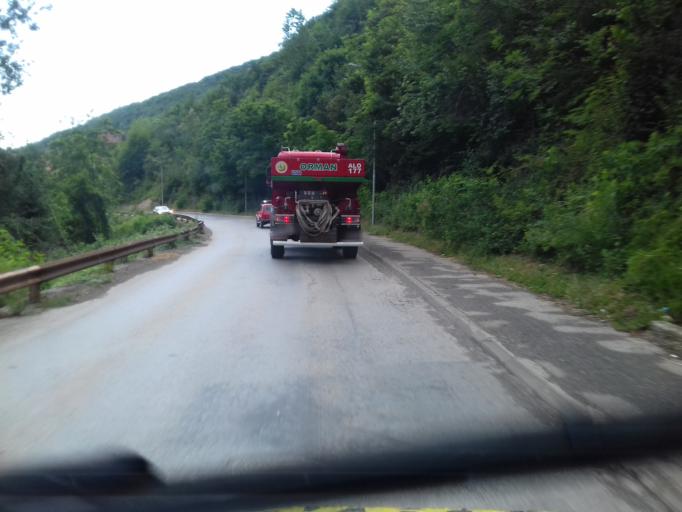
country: BA
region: Federation of Bosnia and Herzegovina
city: Visoko
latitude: 43.9701
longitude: 18.1850
